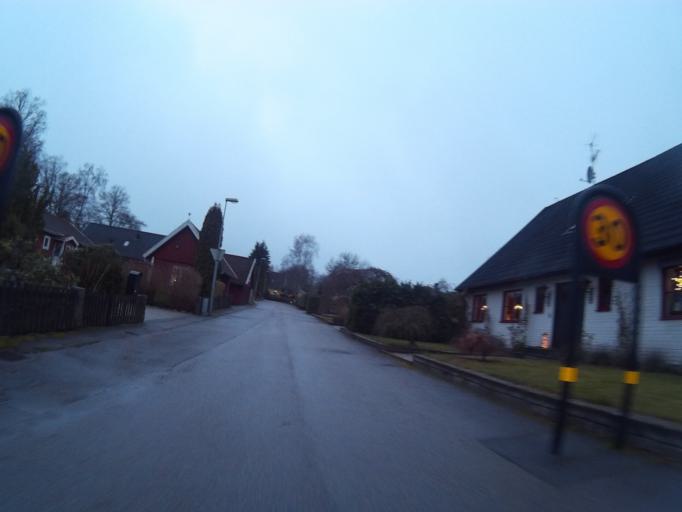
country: SE
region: Kronoberg
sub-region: Vaxjo Kommun
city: Vaexjoe
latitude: 56.9038
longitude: 14.7387
